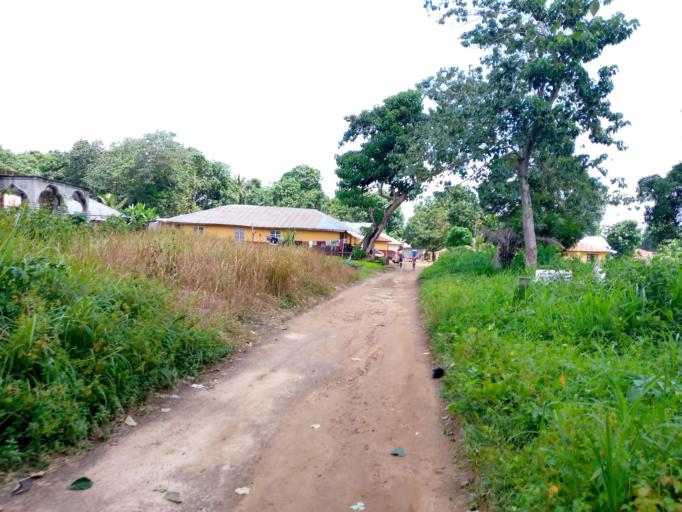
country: SL
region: Northern Province
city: Magburaka
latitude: 8.7311
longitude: -11.9426
